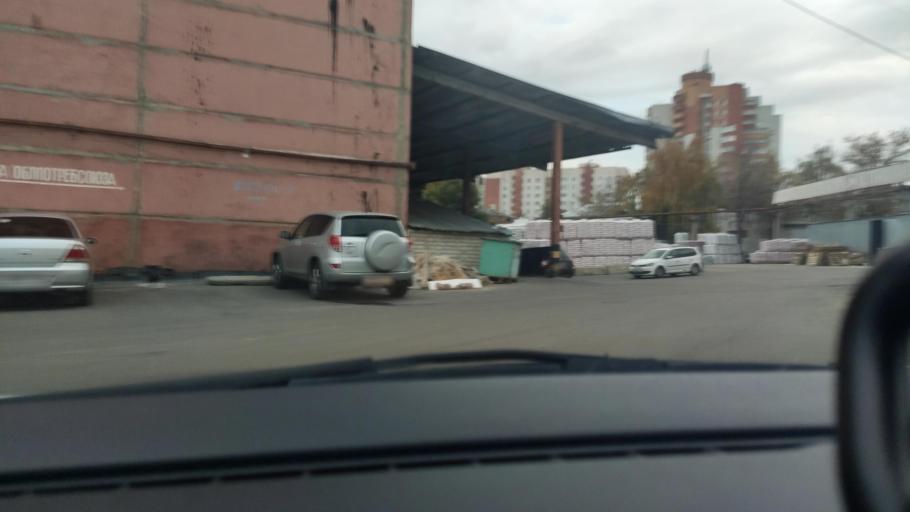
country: RU
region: Voronezj
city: Voronezh
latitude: 51.6649
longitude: 39.1572
